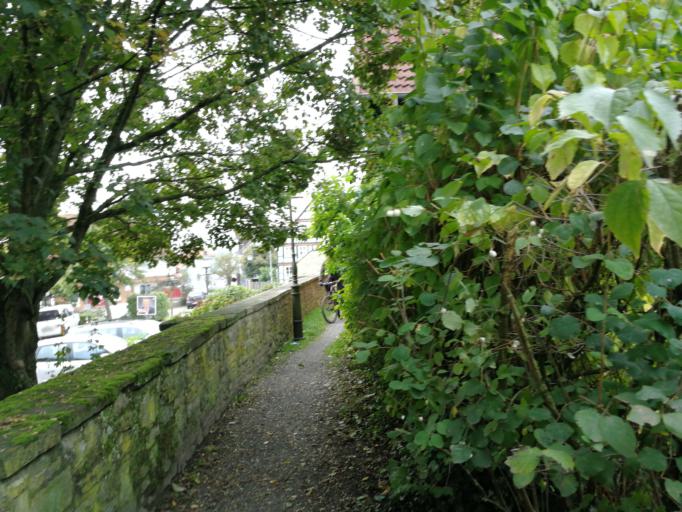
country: DE
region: Lower Saxony
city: Bad Munder am Deister
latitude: 52.1968
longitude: 9.4655
